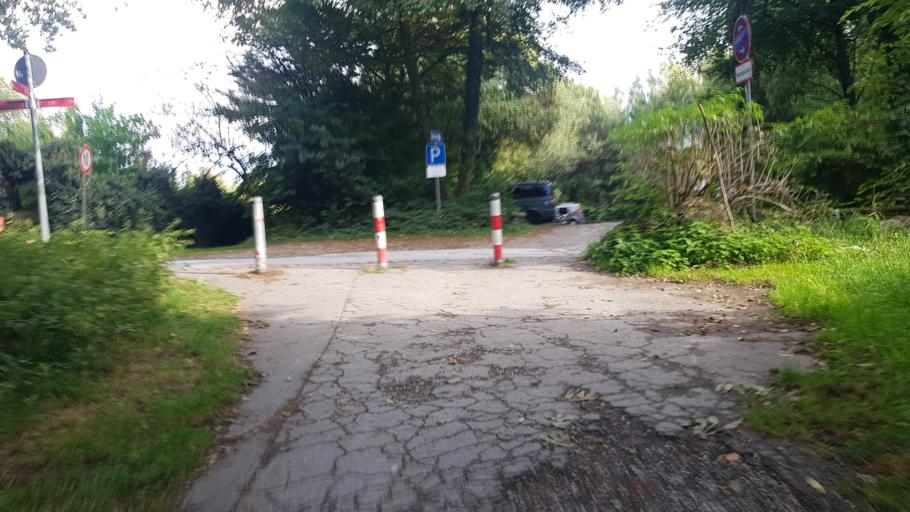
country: DE
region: Baden-Wuerttemberg
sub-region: Tuebingen Region
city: Immenstaad am Bodensee
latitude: 47.6672
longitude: 9.4210
